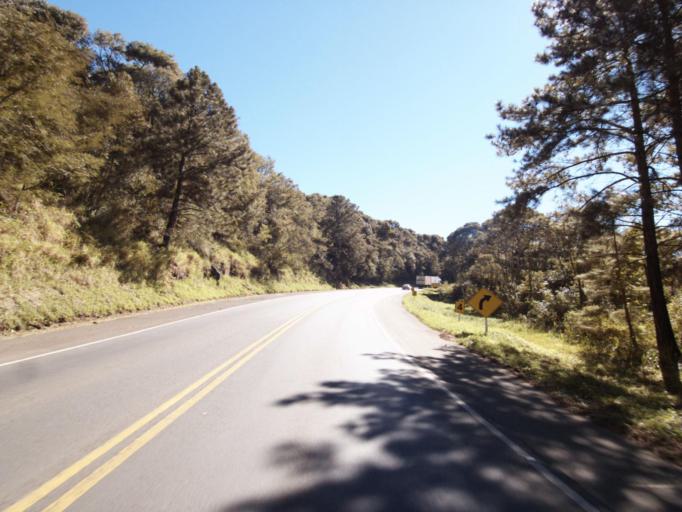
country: BR
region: Santa Catarina
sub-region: Joacaba
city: Joacaba
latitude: -26.9901
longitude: -51.7530
